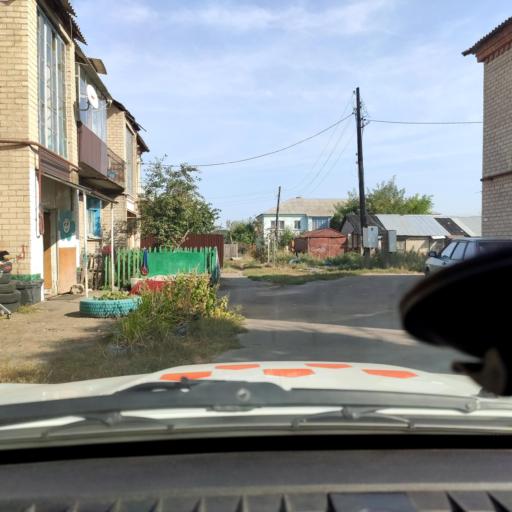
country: RU
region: Voronezj
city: Novaya Usman'
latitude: 51.6532
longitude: 39.3354
